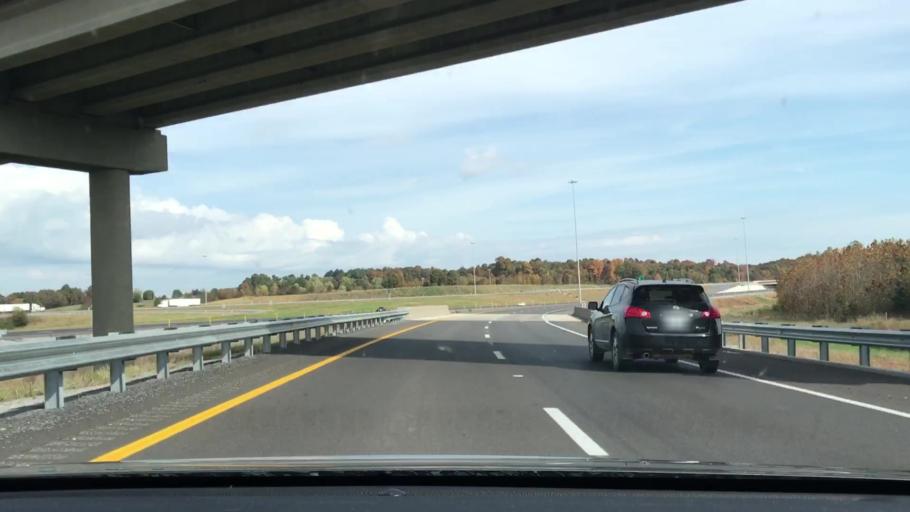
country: US
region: Kentucky
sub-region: Marshall County
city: Calvert City
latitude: 36.9867
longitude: -88.3454
